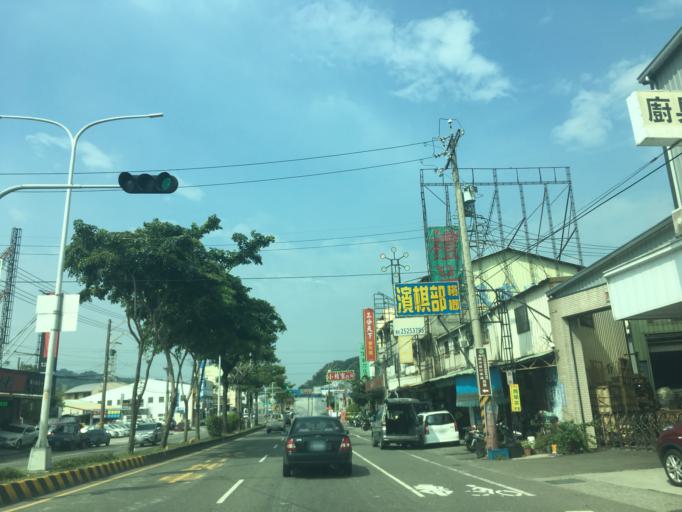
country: TW
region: Taiwan
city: Fengyuan
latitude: 24.2659
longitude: 120.7469
